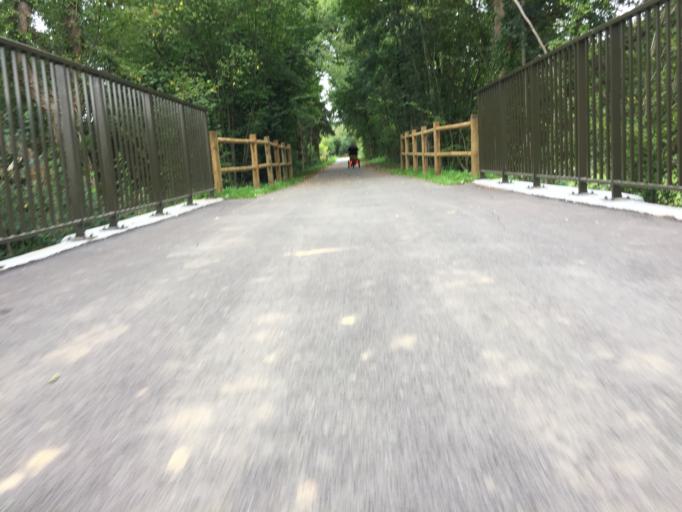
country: FR
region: Picardie
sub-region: Departement de l'Oise
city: Saint-Paul
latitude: 49.4011
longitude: 2.0110
